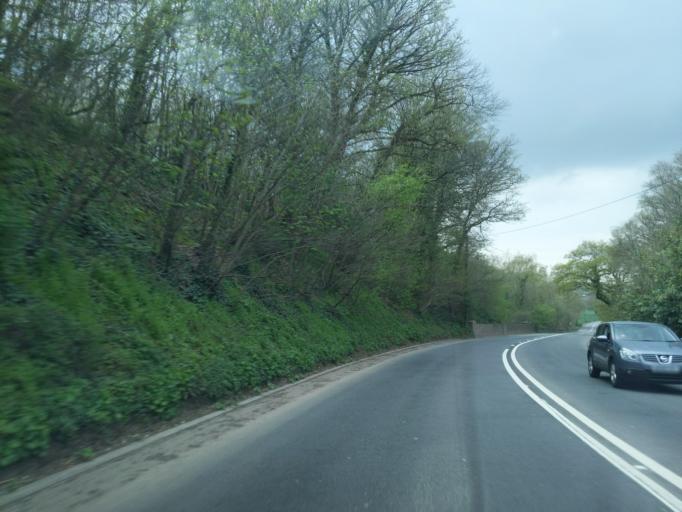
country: GB
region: England
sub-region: Devon
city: Crediton
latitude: 50.7797
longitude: -3.6212
